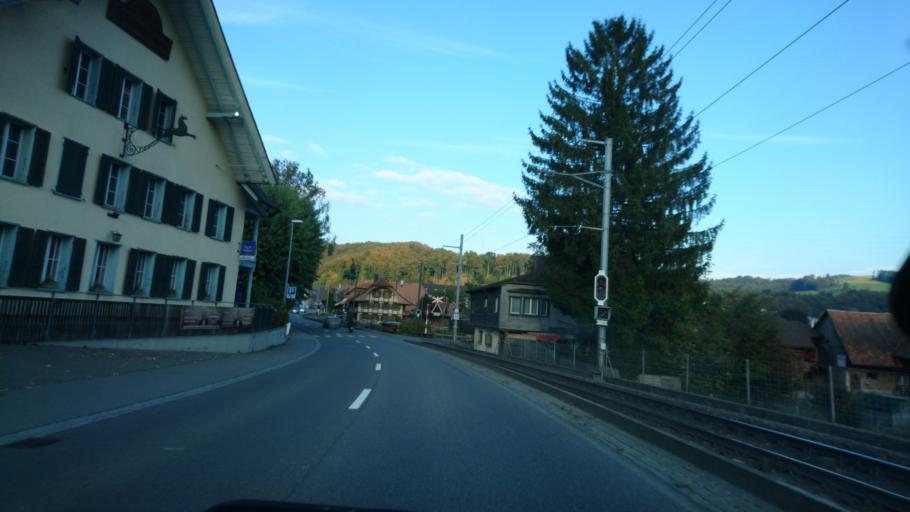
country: CH
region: Bern
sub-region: Bern-Mittelland District
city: Vechigen
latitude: 46.9526
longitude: 7.5437
